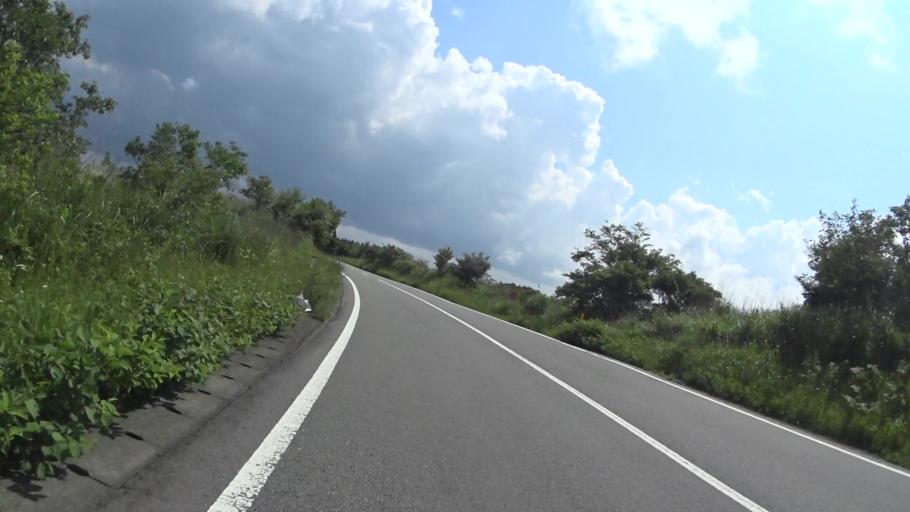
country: JP
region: Kumamoto
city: Aso
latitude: 33.0554
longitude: 131.1747
